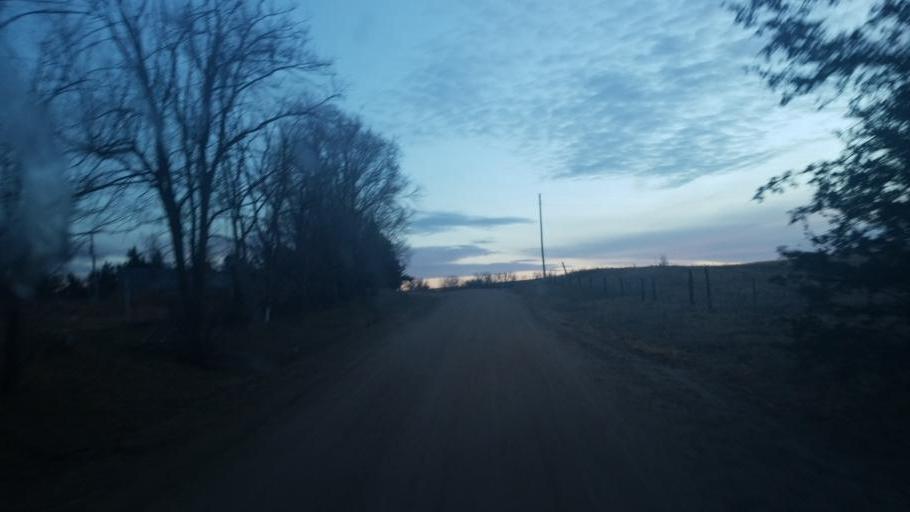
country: US
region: Nebraska
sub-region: Knox County
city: Center
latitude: 42.6168
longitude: -97.8379
